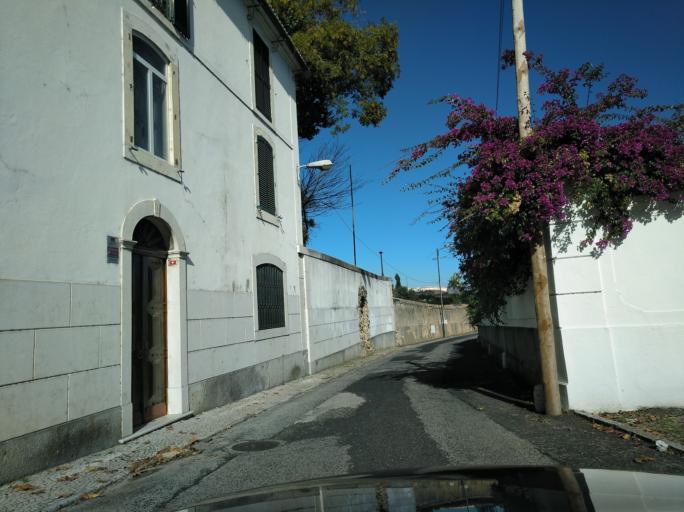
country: PT
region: Lisbon
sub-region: Lisbon
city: Lisbon
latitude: 38.7333
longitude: -9.1098
